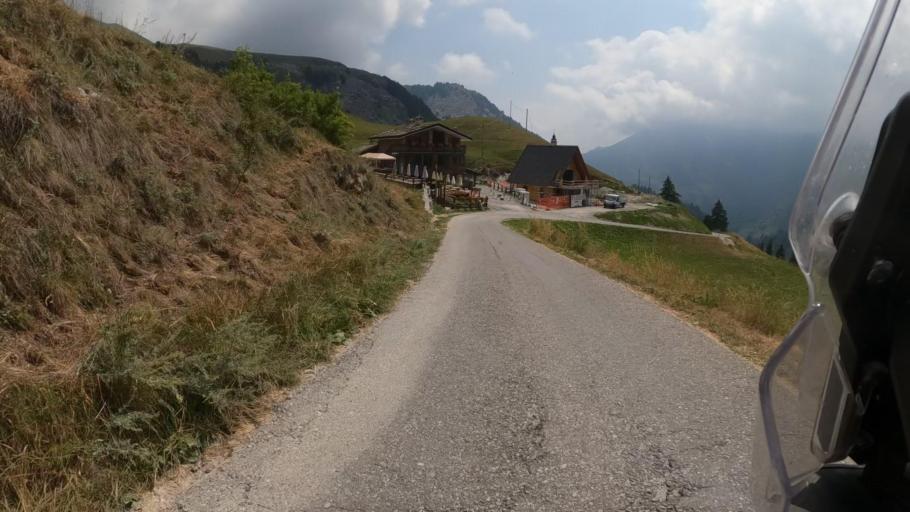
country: IT
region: Piedmont
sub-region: Provincia di Cuneo
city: Campomolino
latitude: 44.4006
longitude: 7.1676
